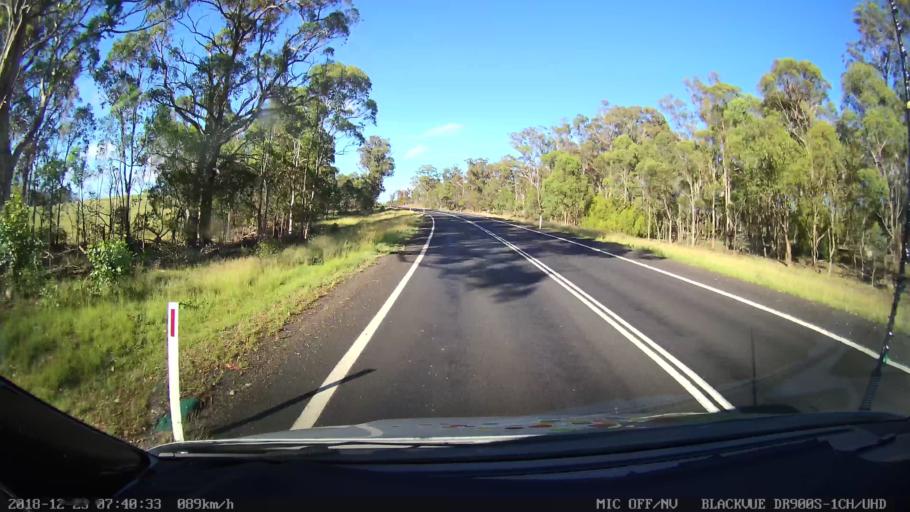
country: AU
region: New South Wales
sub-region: Armidale Dumaresq
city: Enmore
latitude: -30.5144
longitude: 152.0053
